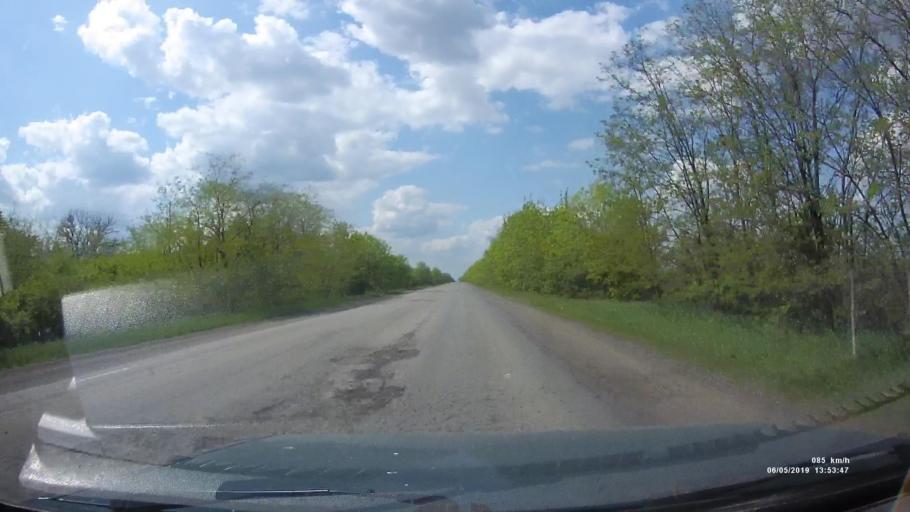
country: RU
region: Rostov
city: Melikhovskaya
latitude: 47.6704
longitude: 40.4570
